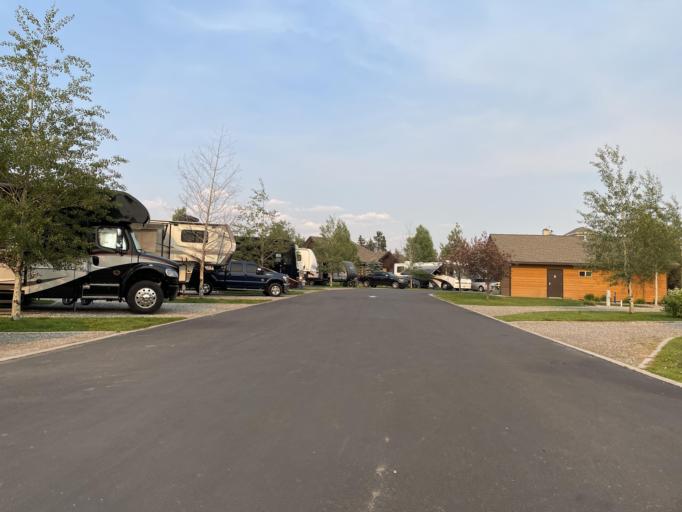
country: US
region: Montana
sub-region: Gallatin County
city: West Yellowstone
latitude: 44.6560
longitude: -111.1053
